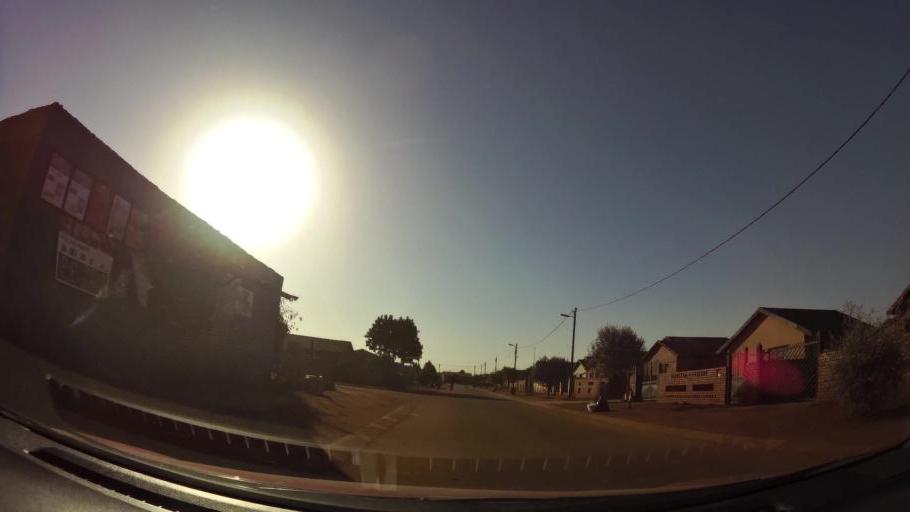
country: ZA
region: Gauteng
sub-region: City of Tshwane Metropolitan Municipality
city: Mabopane
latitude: -25.5896
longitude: 28.0948
